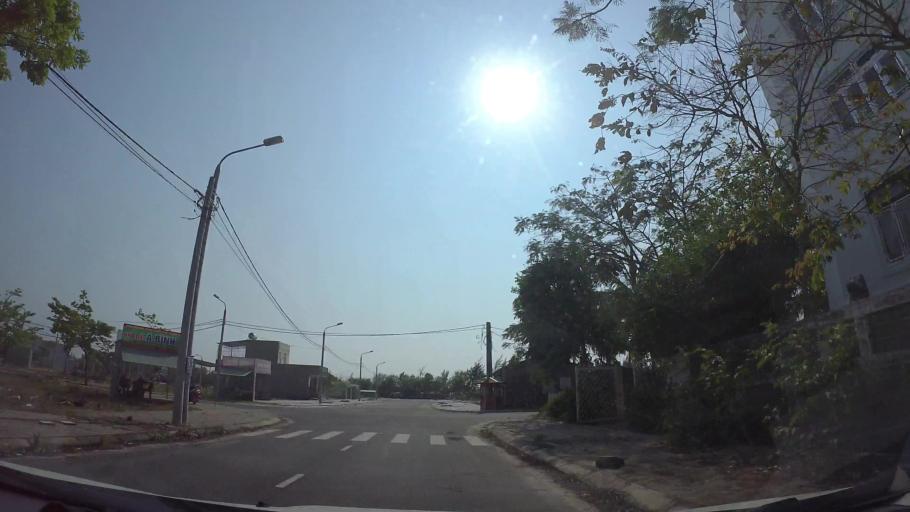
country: VN
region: Da Nang
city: Ngu Hanh Son
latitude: 15.9561
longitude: 108.2798
